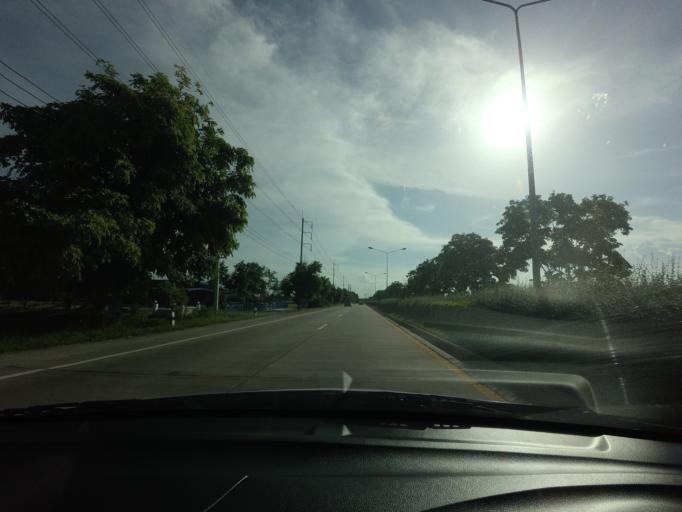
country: TH
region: Suphan Buri
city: Suphan Buri
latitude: 14.4450
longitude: 100.1359
